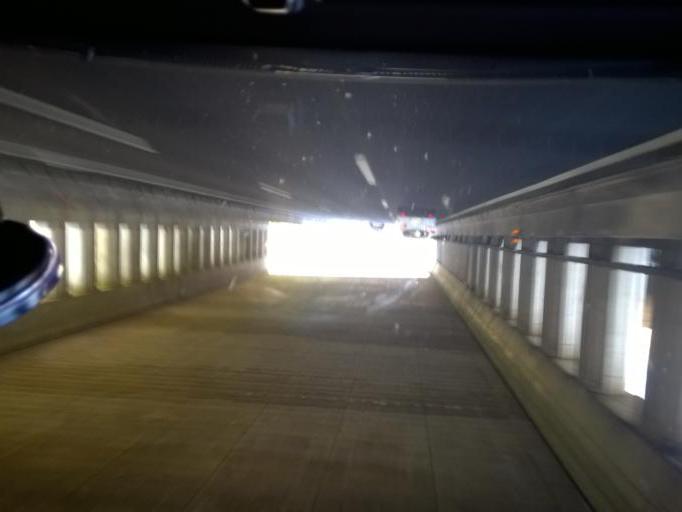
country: IT
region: Emilia-Romagna
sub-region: Provincia di Parma
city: San Prospero
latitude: 44.8231
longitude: 10.3889
